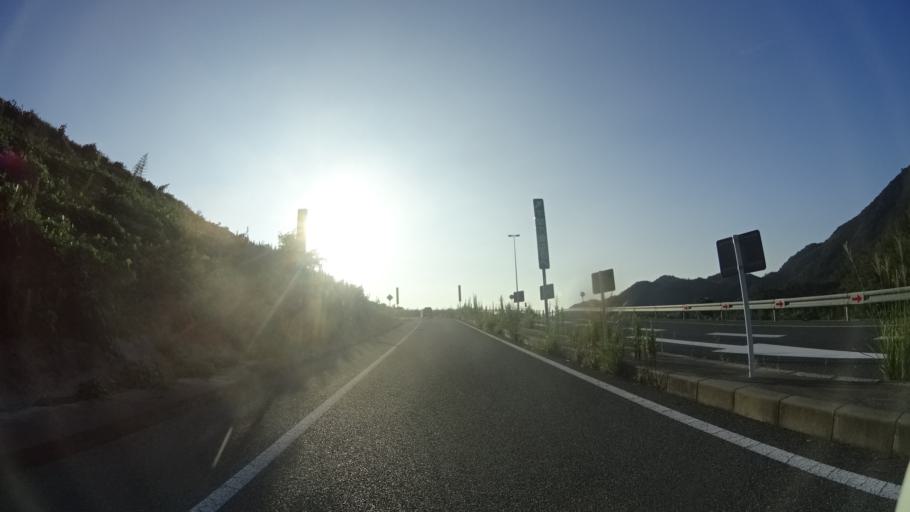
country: JP
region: Yamaguchi
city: Hagi
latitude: 34.3867
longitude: 131.3511
